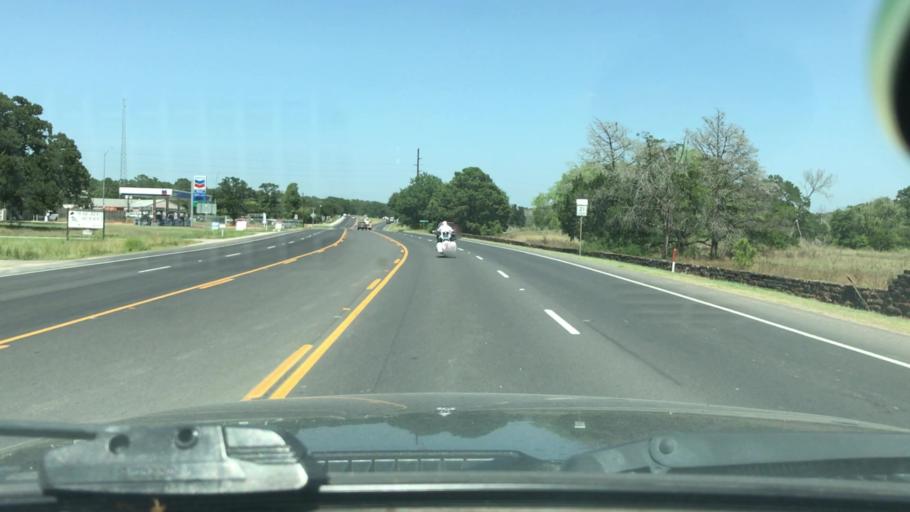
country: US
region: Texas
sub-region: Bastrop County
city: Bastrop
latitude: 30.1112
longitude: -97.2934
